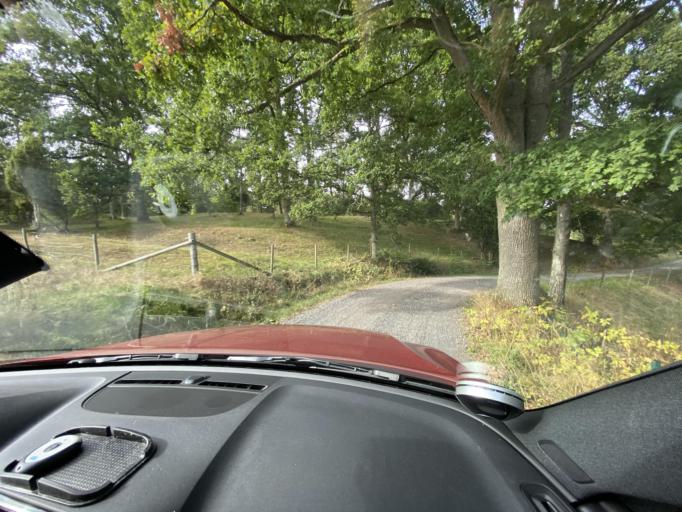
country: SE
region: Skane
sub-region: Hassleholms Kommun
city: Hastveda
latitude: 56.3574
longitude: 13.8795
